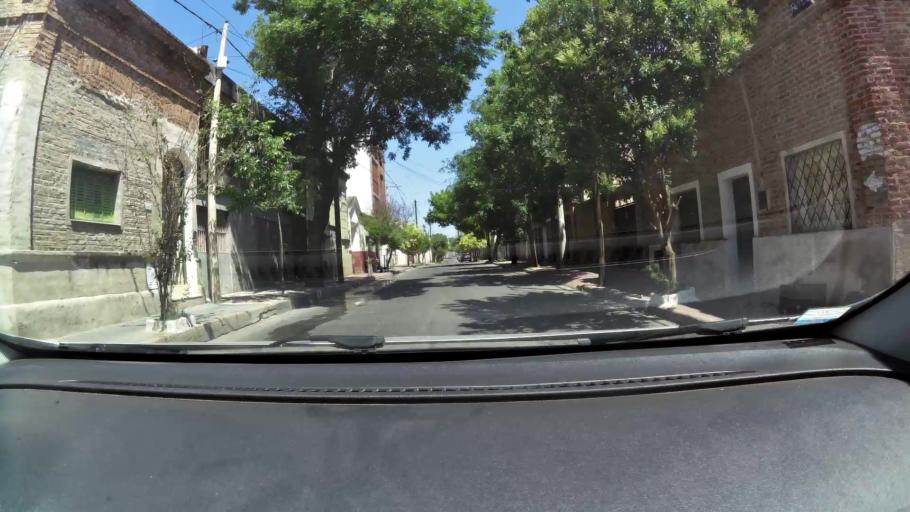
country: AR
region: Cordoba
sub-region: Departamento de Capital
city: Cordoba
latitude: -31.3987
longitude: -64.1953
